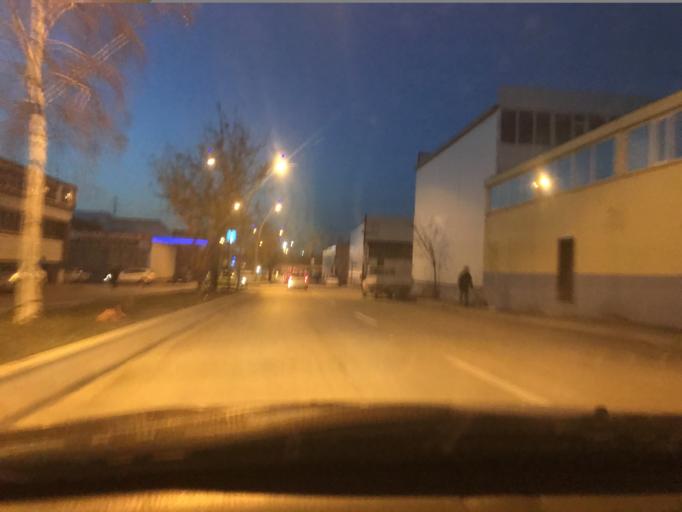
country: TR
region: Ankara
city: Batikent
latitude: 39.9713
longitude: 32.7406
